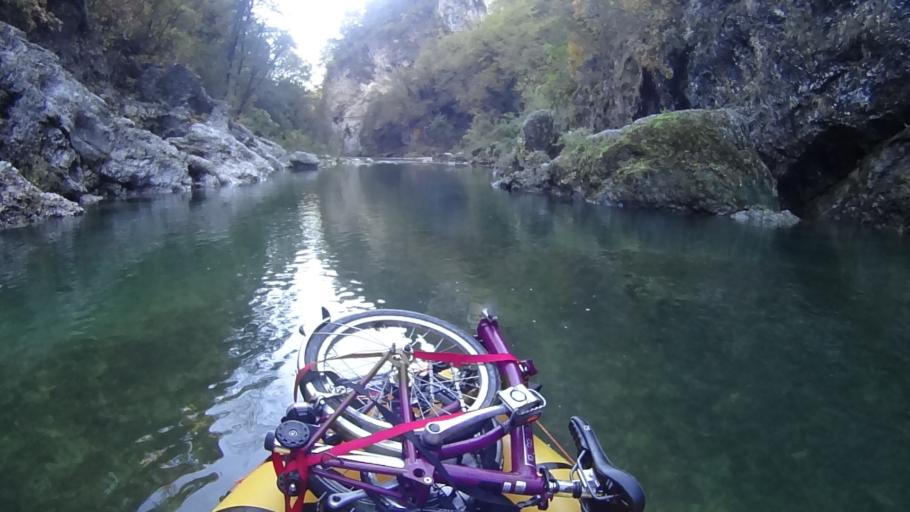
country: IT
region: Veneto
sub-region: Provincia di Vicenza
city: Cogollo del Cengio
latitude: 45.7717
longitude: 11.4255
